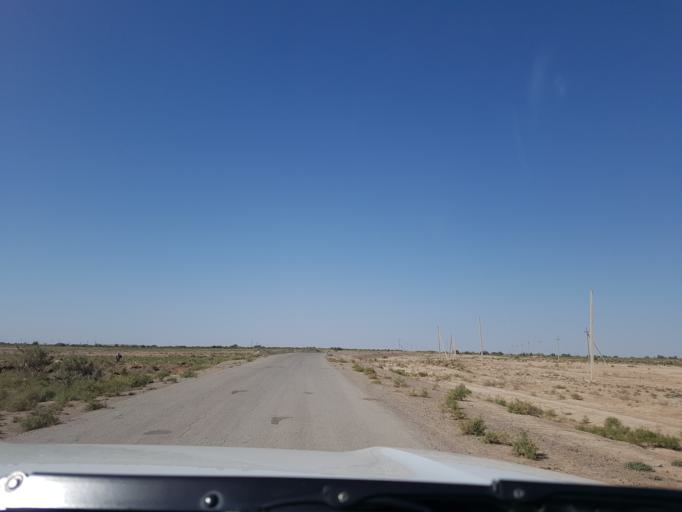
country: IR
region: Razavi Khorasan
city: Sarakhs
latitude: 36.4937
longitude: 61.2543
